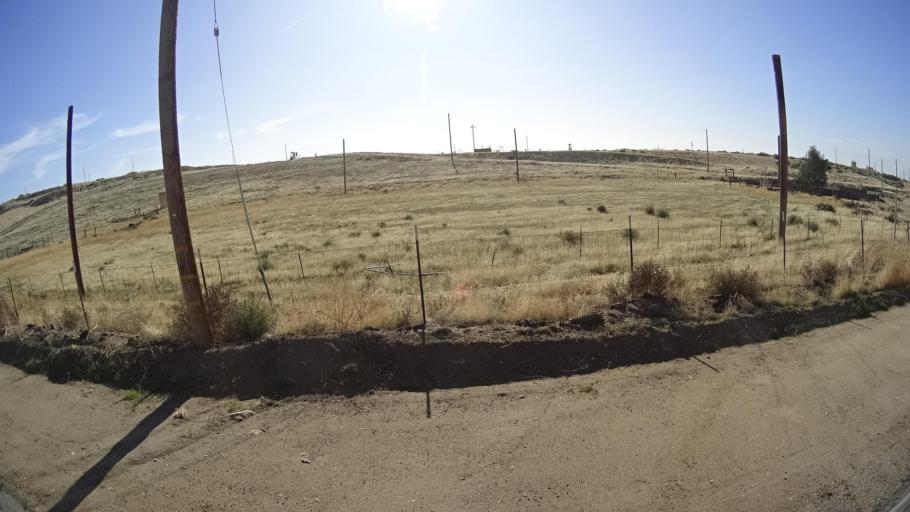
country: US
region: California
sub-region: Kern County
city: Lamont
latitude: 35.3755
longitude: -118.8405
